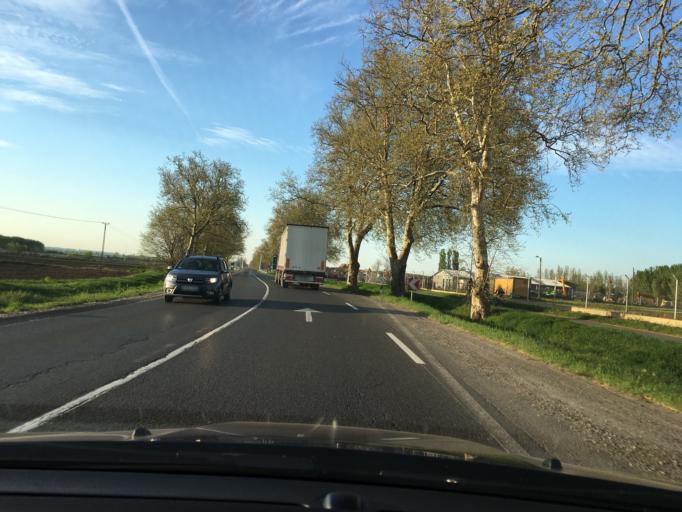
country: HU
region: Hajdu-Bihar
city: Mikepercs
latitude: 47.4587
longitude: 21.6367
